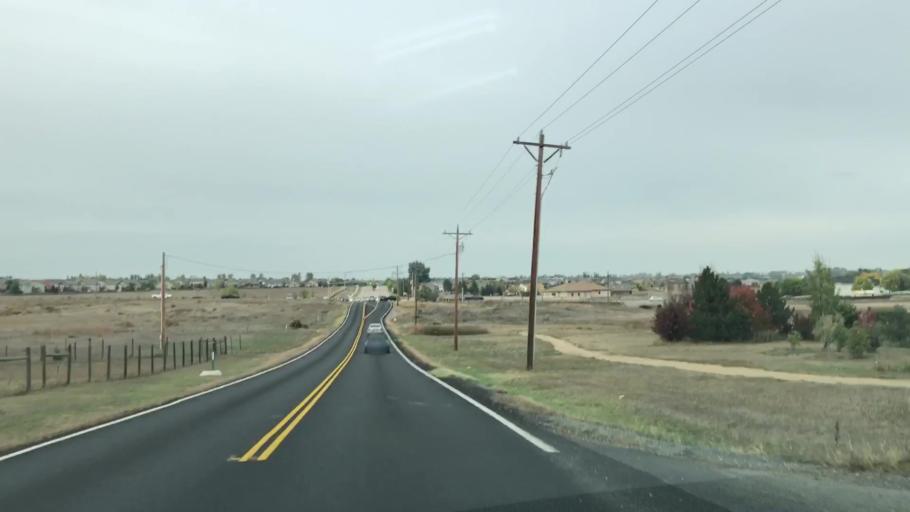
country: US
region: Colorado
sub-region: Larimer County
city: Loveland
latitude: 40.4776
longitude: -105.0583
